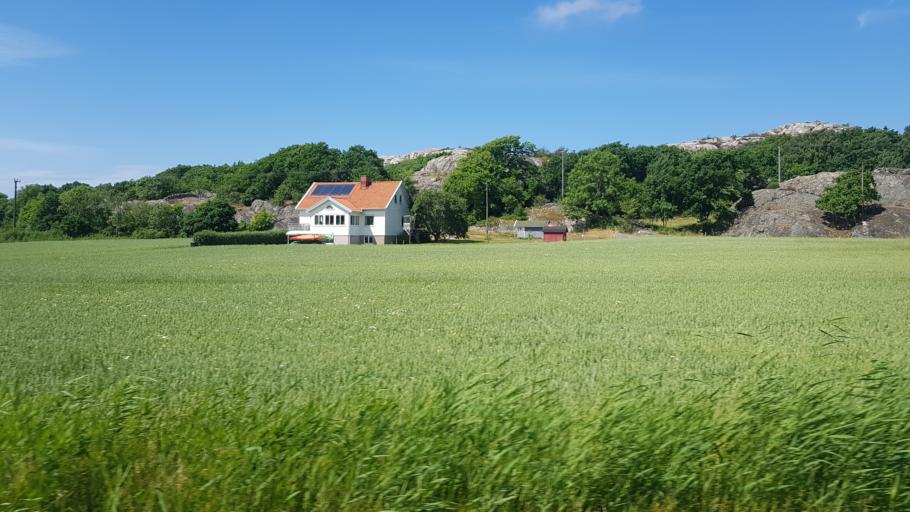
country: SE
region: Vaestra Goetaland
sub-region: Tjorns Kommun
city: Skaerhamn
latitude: 57.9749
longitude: 11.5621
